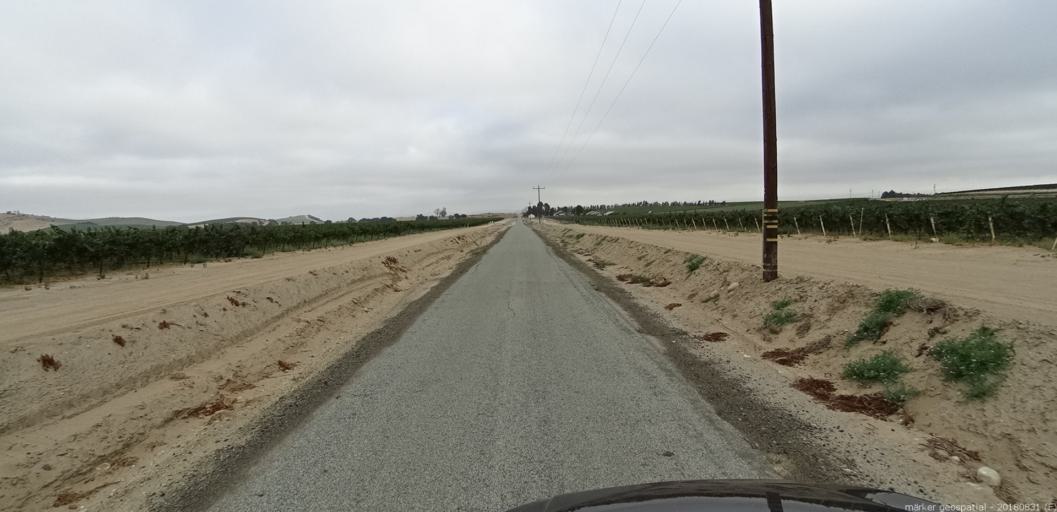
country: US
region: California
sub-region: Monterey County
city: King City
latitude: 36.1166
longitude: -121.0874
